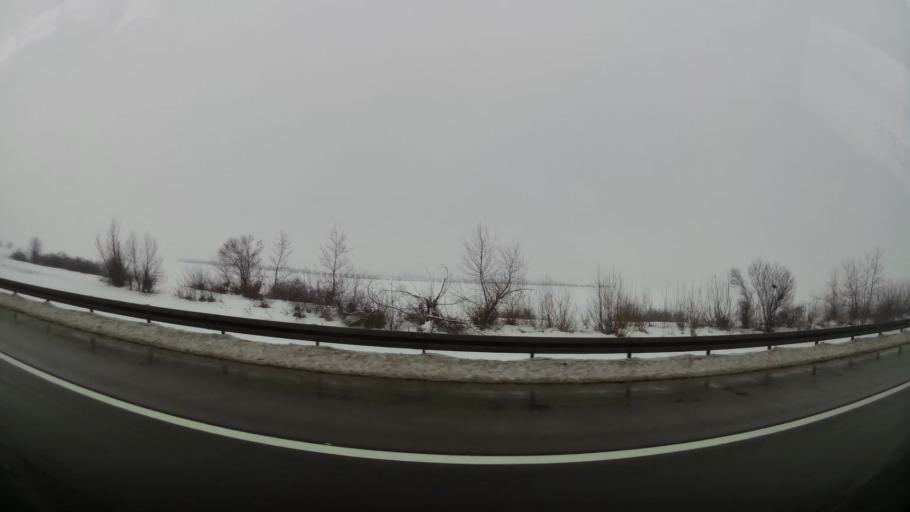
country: RS
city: Dobanovci
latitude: 44.8282
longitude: 20.2517
